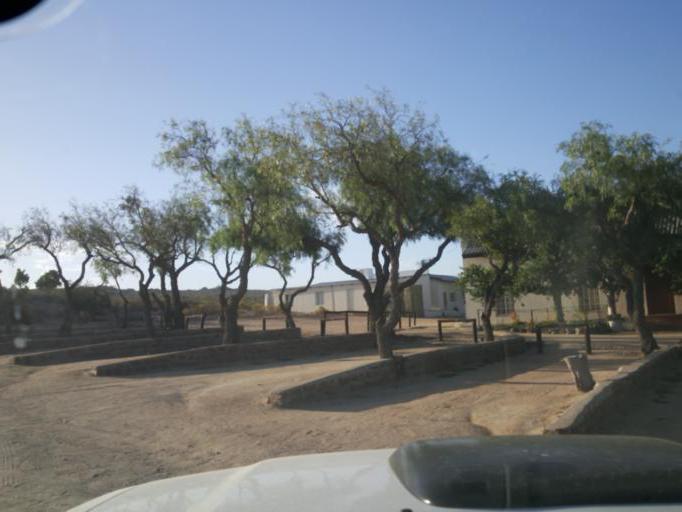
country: ZA
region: Northern Cape
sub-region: Namakwa District Municipality
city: Springbok
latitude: -29.7016
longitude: 17.6657
